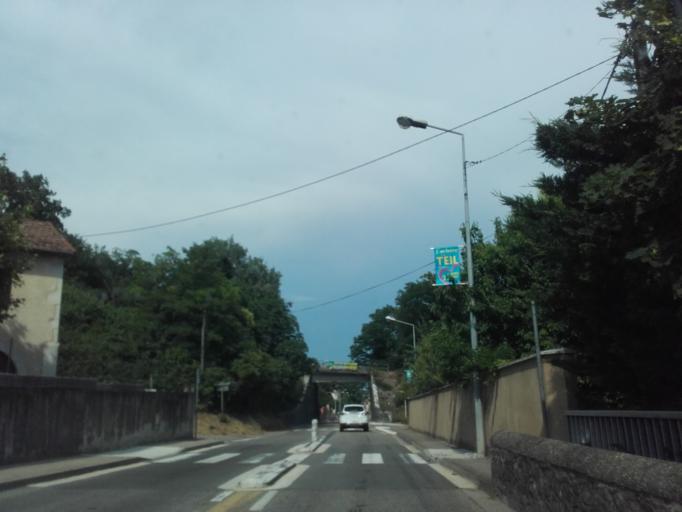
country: FR
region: Rhone-Alpes
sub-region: Departement de l'Ardeche
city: Le Teil
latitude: 44.5434
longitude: 4.6745
